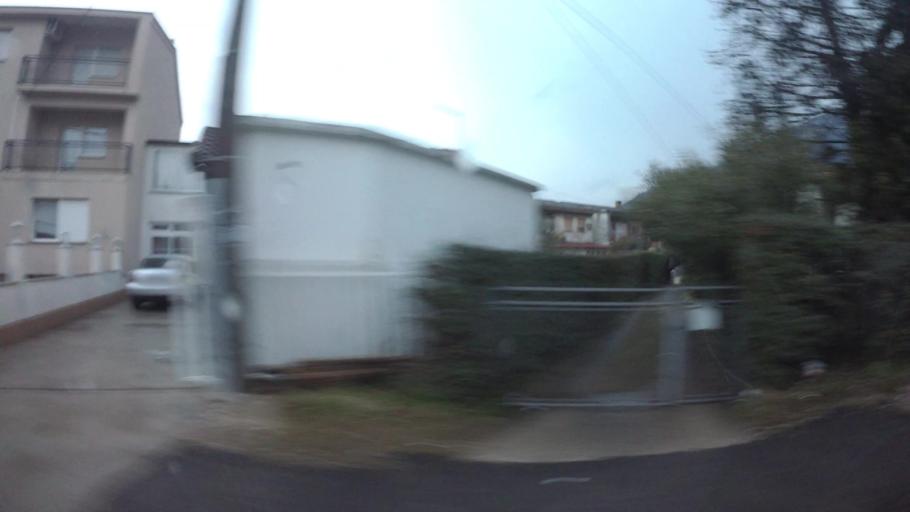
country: BA
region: Federation of Bosnia and Herzegovina
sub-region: Hercegovacko-Bosanski Kanton
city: Mostar
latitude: 43.3573
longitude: 17.8012
